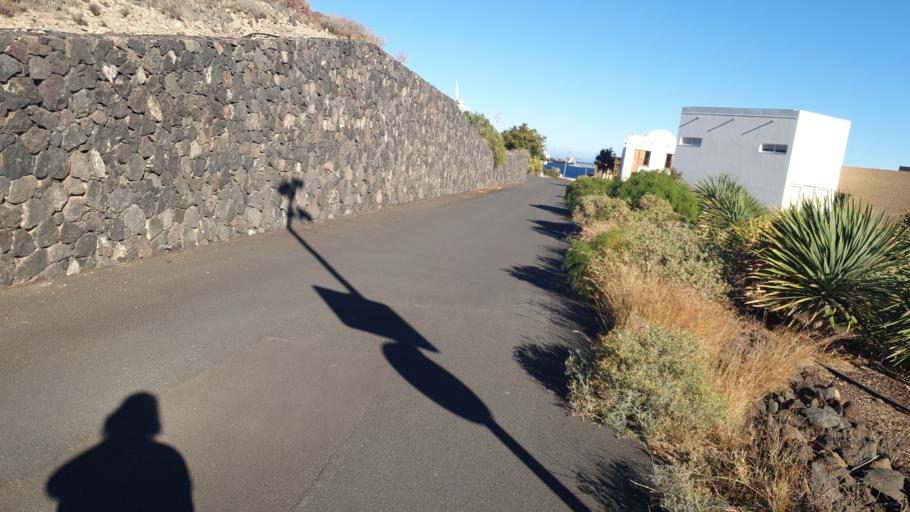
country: ES
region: Canary Islands
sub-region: Provincia de Santa Cruz de Tenerife
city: San Isidro
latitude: 28.0682
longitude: -16.5112
